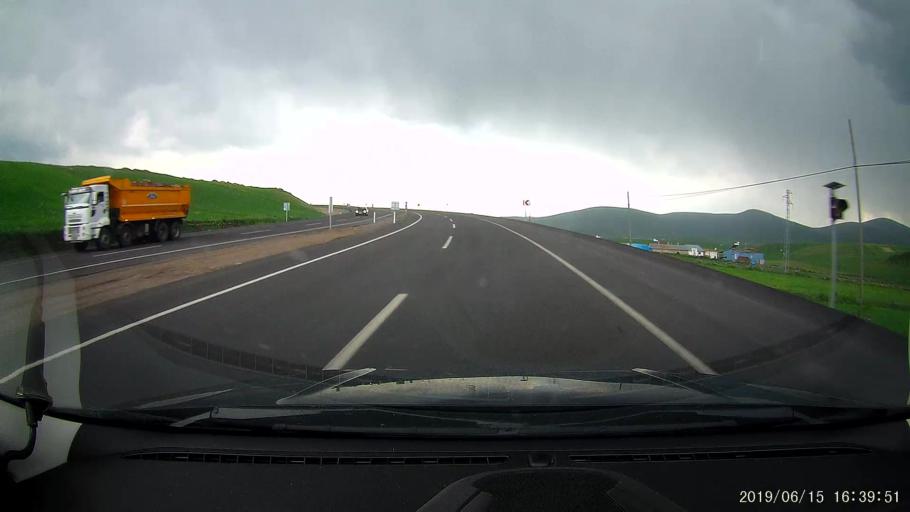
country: TR
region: Ardahan
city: Haskoy
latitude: 40.9779
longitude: 42.8937
